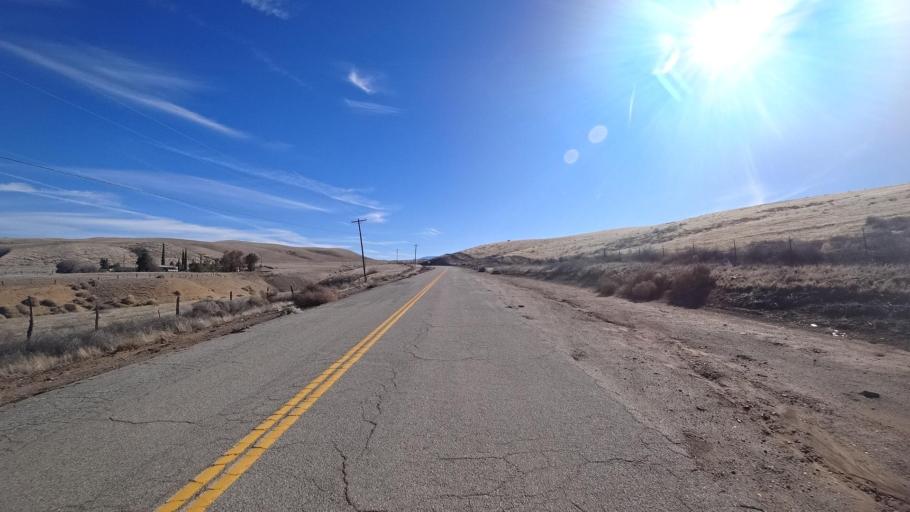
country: US
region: California
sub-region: Kern County
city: Maricopa
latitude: 34.9603
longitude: -119.4464
